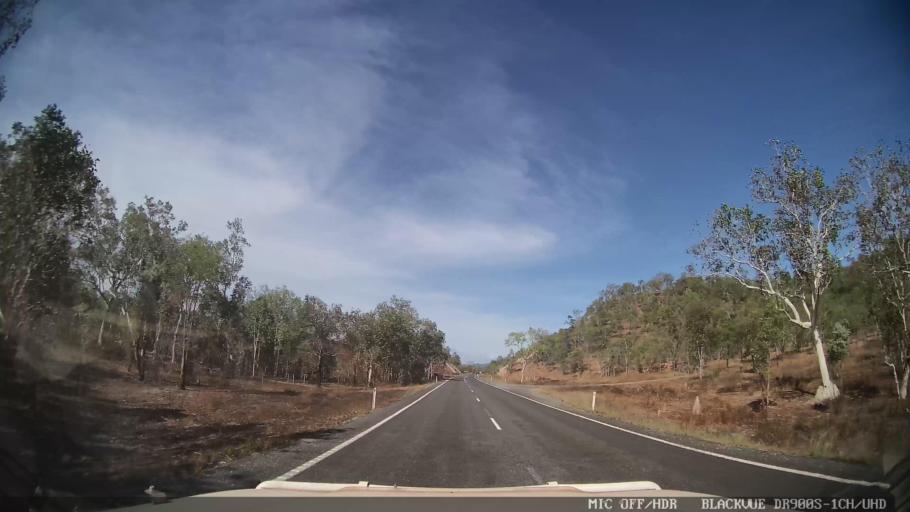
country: AU
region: Queensland
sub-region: Cook
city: Cooktown
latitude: -15.6916
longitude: 145.1155
